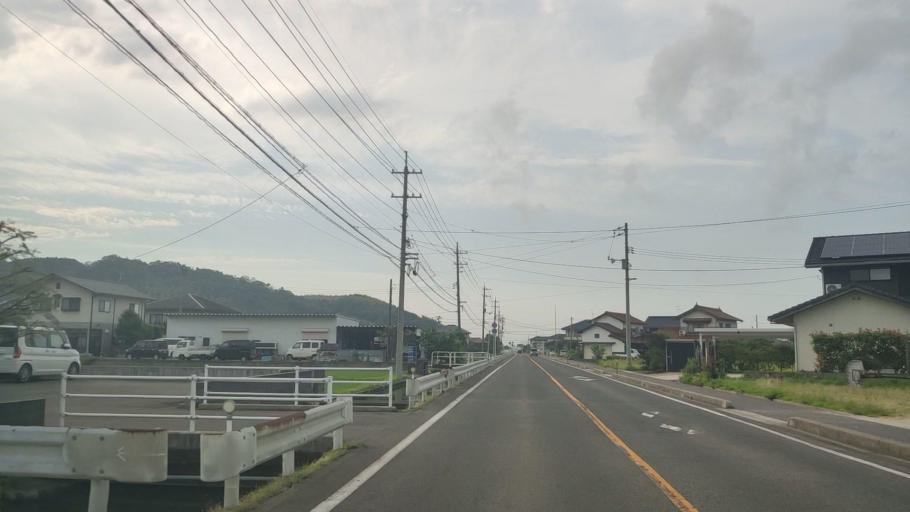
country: JP
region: Tottori
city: Kurayoshi
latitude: 35.4613
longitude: 133.8344
